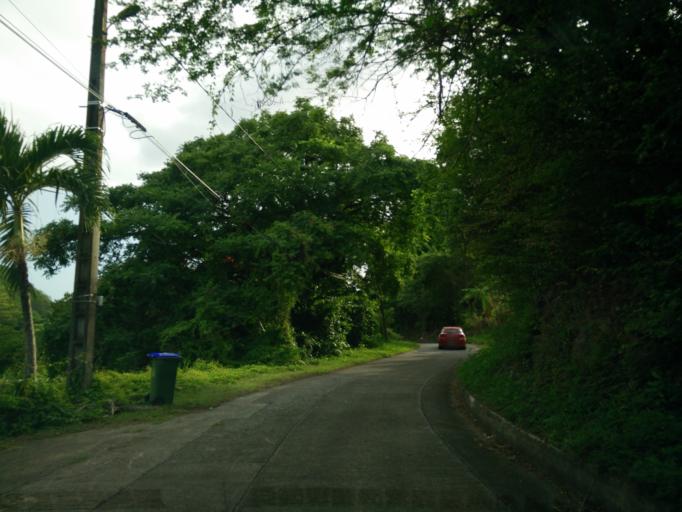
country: MQ
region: Martinique
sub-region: Martinique
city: Saint-Pierre
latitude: 14.7137
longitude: -61.1727
